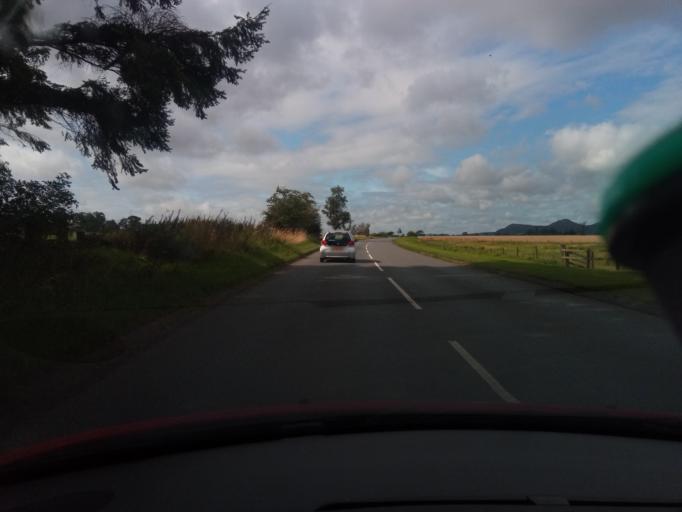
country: GB
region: Scotland
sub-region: The Scottish Borders
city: Saint Boswells
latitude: 55.5667
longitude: -2.5907
